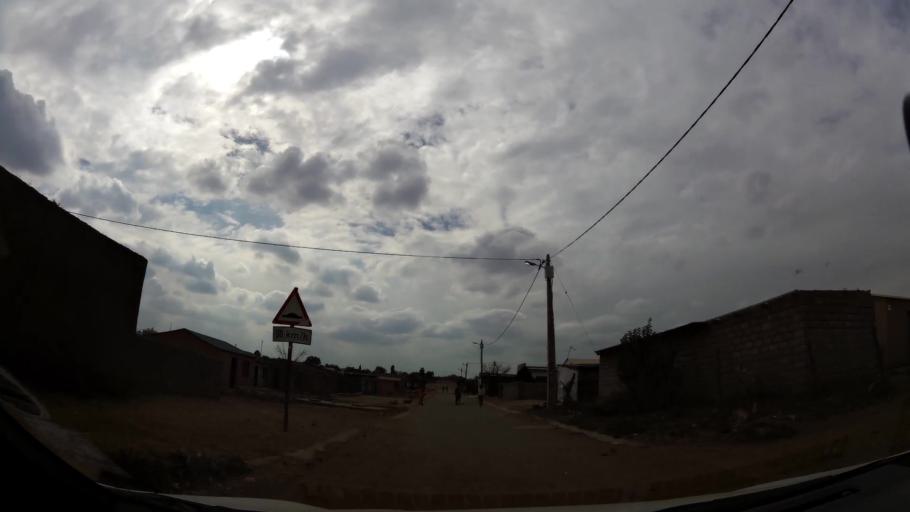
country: ZA
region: Gauteng
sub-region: Ekurhuleni Metropolitan Municipality
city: Germiston
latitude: -26.3876
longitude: 28.1317
